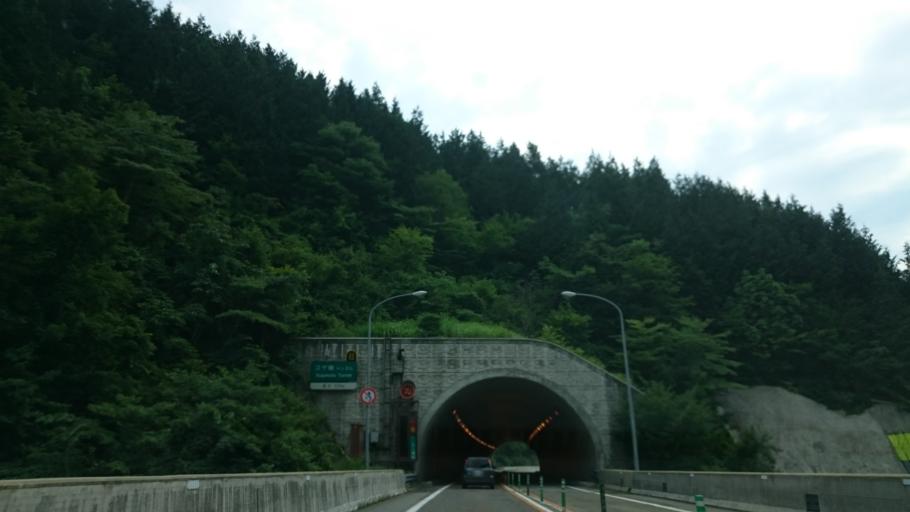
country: JP
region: Gifu
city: Takayama
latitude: 36.0303
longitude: 137.0101
